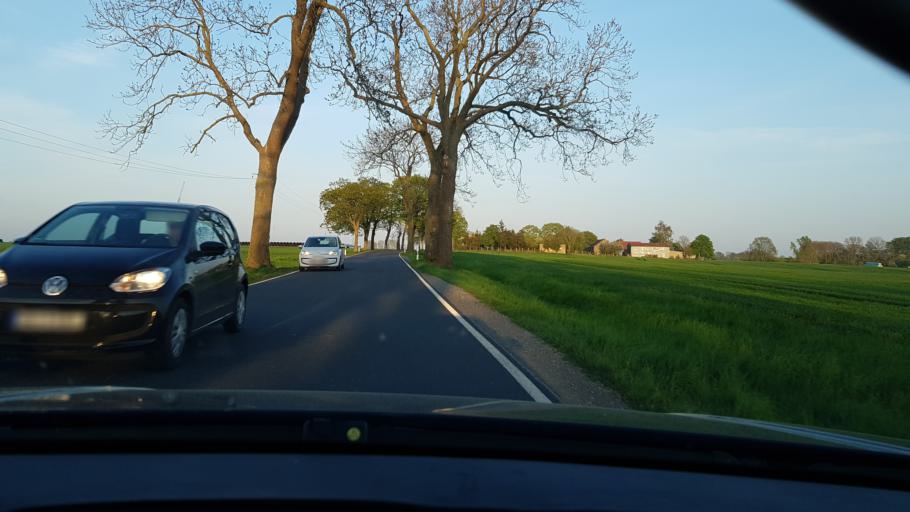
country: DE
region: Mecklenburg-Vorpommern
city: Alt-Sanitz
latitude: 53.8932
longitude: 13.6046
